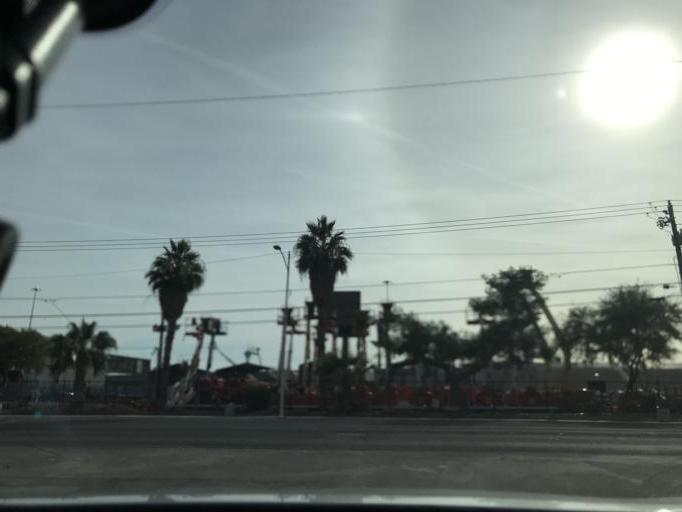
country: US
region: Nevada
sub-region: Clark County
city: Las Vegas
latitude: 36.1774
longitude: -115.1671
